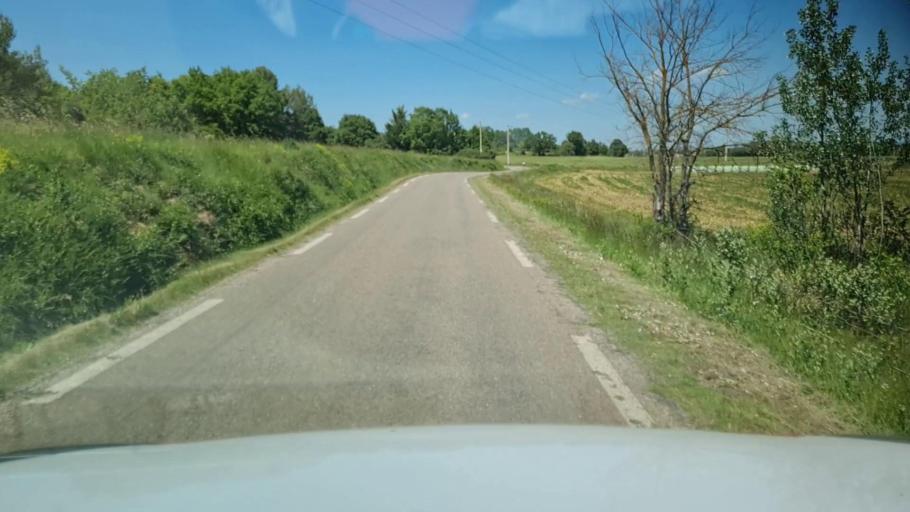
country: FR
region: Languedoc-Roussillon
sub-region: Departement du Gard
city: Saint-Mamert-du-Gard
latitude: 43.8957
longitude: 4.1892
